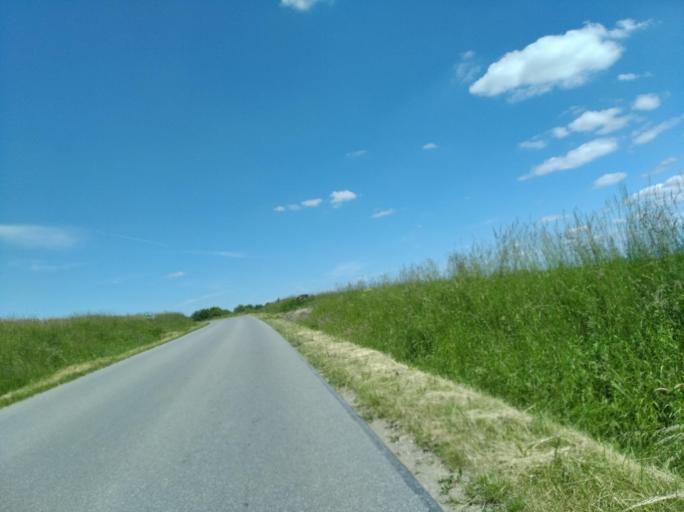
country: PL
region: Subcarpathian Voivodeship
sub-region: Powiat jasielski
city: Osiek Jasielski
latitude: 49.6543
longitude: 21.5302
